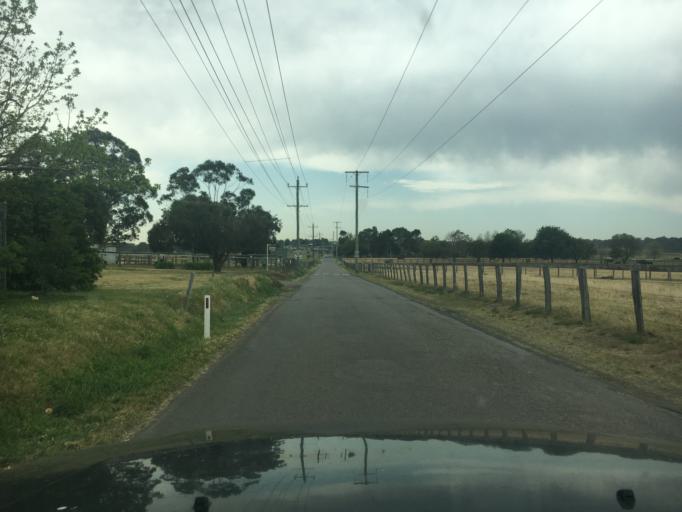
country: AU
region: New South Wales
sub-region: Maitland Municipality
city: Maitland
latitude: -32.7505
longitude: 151.5609
